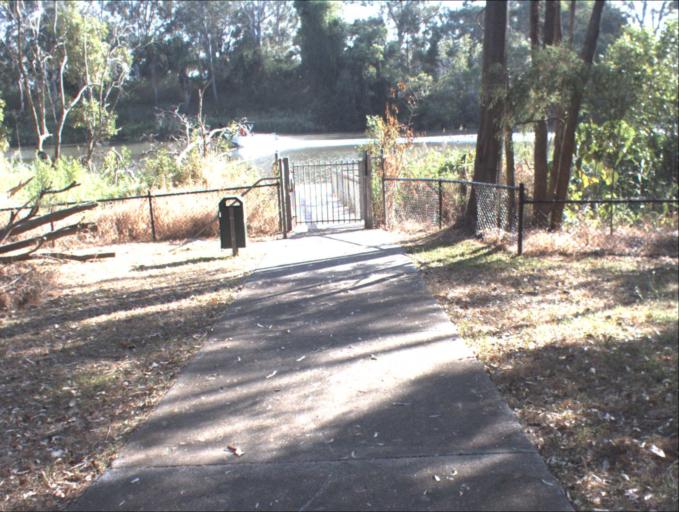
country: AU
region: Queensland
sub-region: Logan
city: Beenleigh
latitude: -27.7016
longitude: 153.1871
